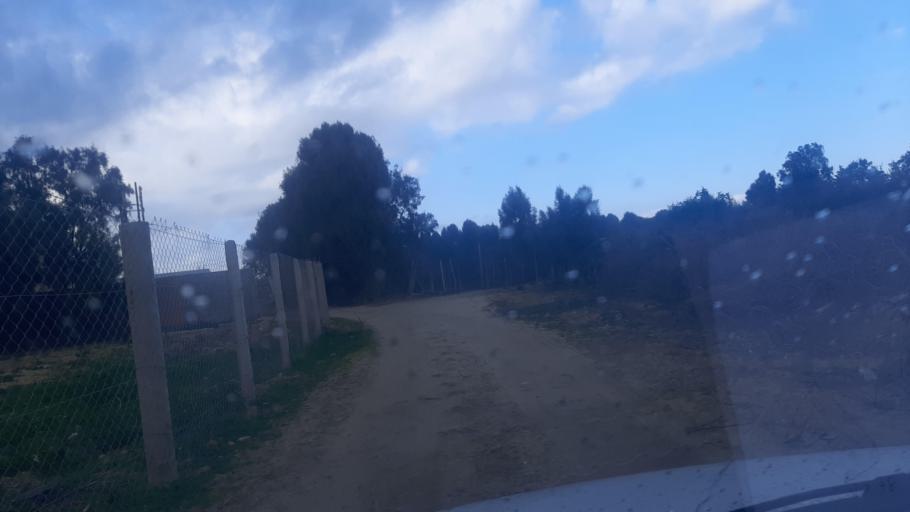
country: TN
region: Nabul
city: Qurbus
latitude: 36.7450
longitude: 10.5259
